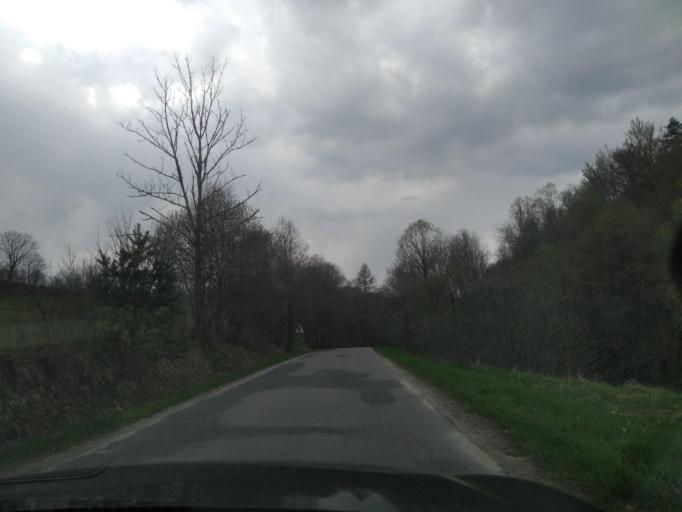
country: PL
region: Subcarpathian Voivodeship
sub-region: Powiat leski
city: Baligrod
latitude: 49.3475
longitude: 22.2462
